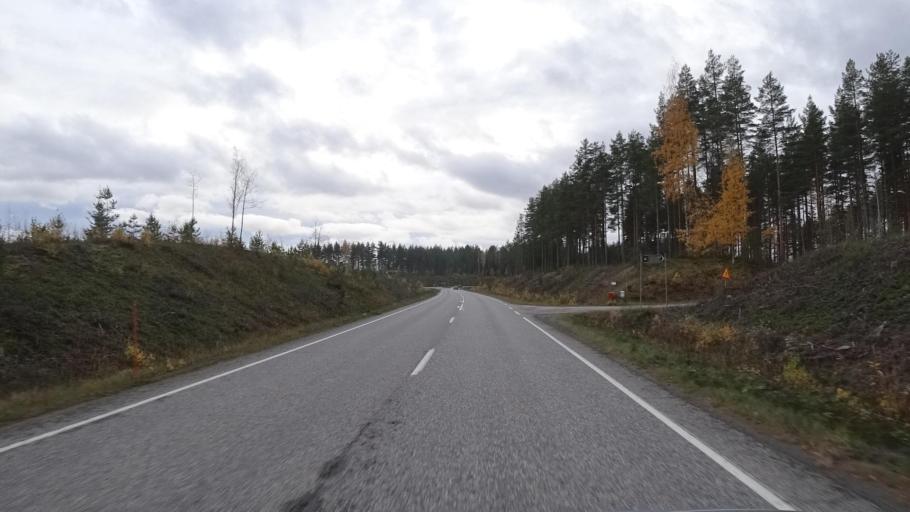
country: FI
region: Central Finland
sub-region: Joutsa
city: Joutsa
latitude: 61.7513
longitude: 26.1360
